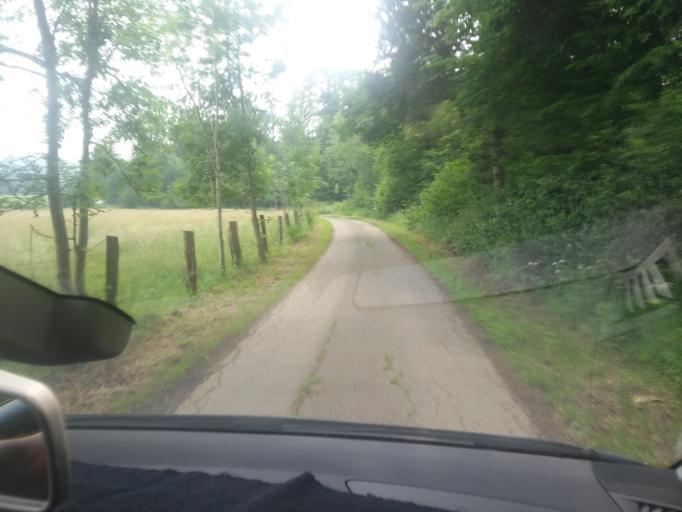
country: BE
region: Wallonia
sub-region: Province du Luxembourg
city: Attert
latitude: 49.6946
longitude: 5.7473
